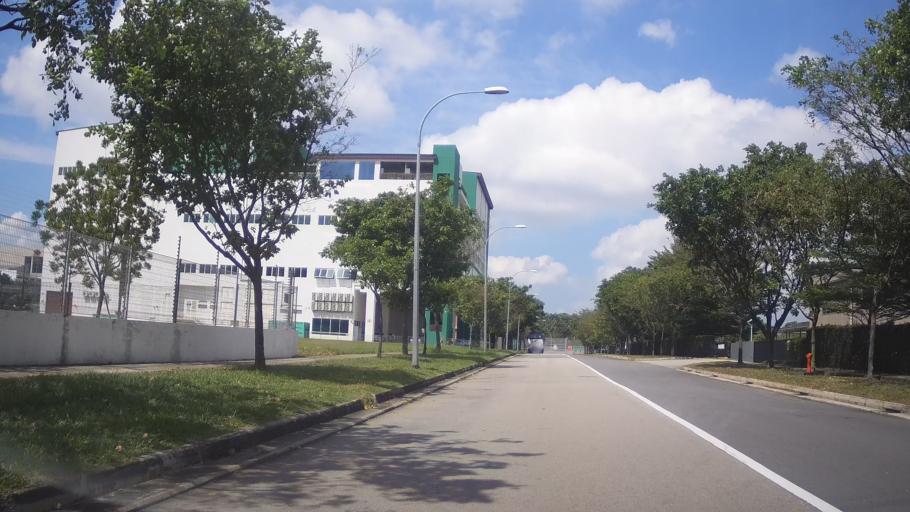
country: SG
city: Singapore
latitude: 1.3233
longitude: 103.7132
